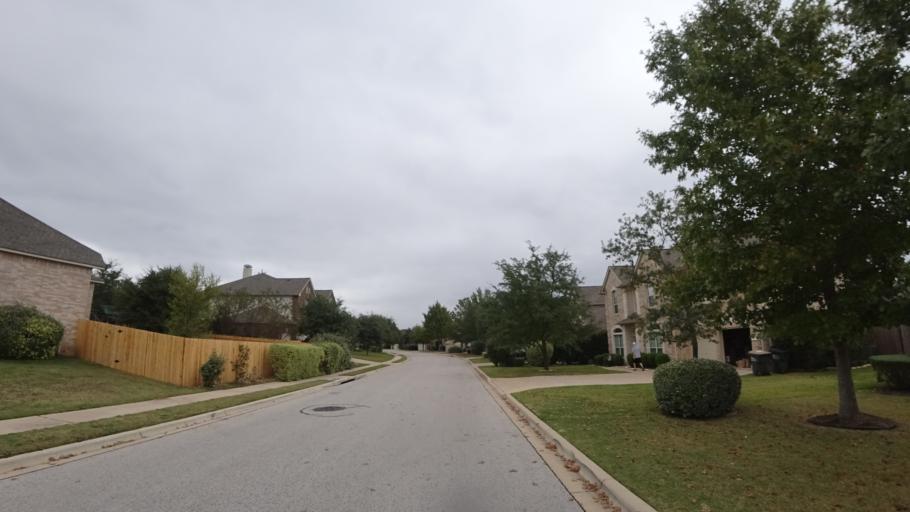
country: US
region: Texas
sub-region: Travis County
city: Bee Cave
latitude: 30.3528
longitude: -97.9034
